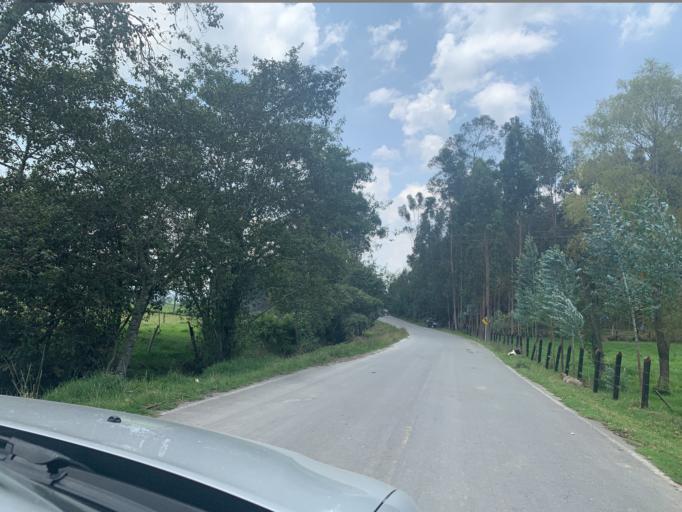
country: CO
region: Boyaca
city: Chiquinquira
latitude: 5.5395
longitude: -73.7485
